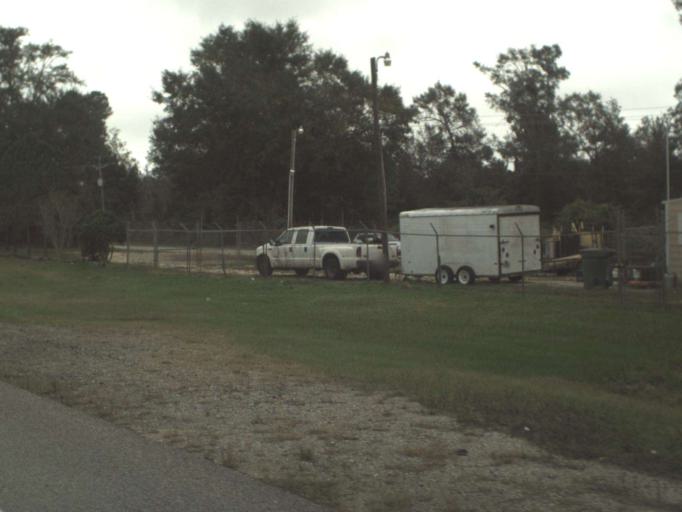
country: US
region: Florida
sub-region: Escambia County
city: Gonzalez
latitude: 30.5731
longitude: -87.2917
